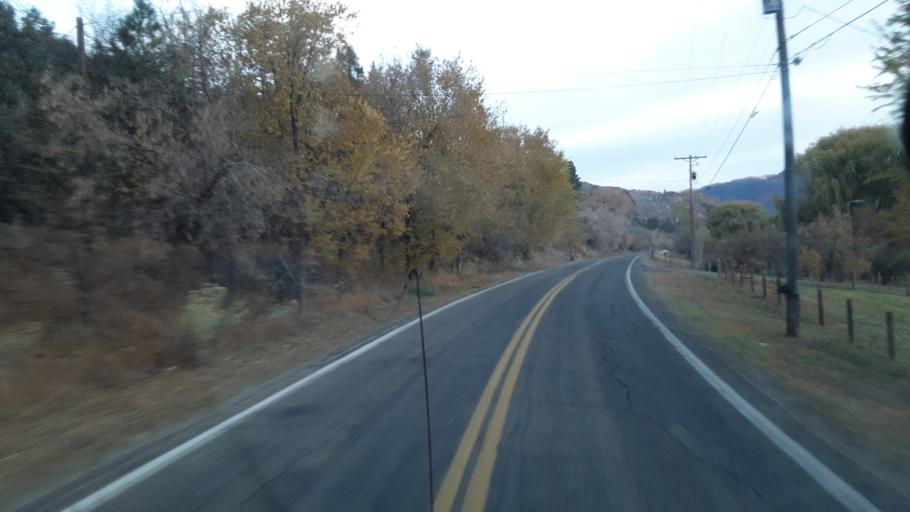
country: US
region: Colorado
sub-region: La Plata County
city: Durango
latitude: 37.3713
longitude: -107.8542
